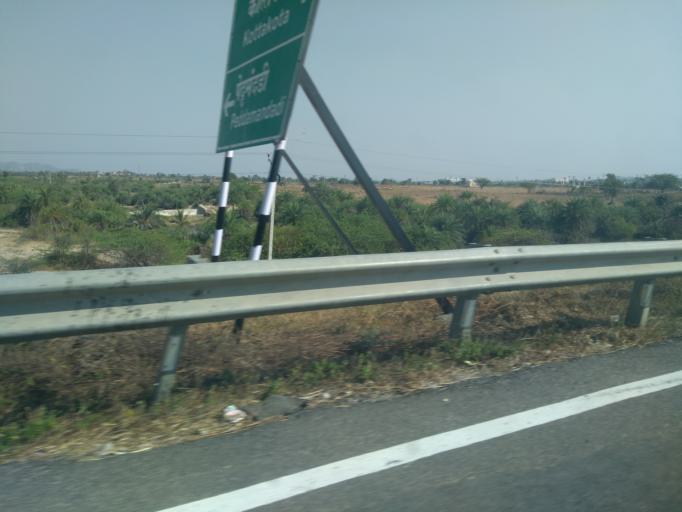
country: IN
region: Telangana
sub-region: Mahbubnagar
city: Wanparti
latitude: 16.4519
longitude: 77.9371
